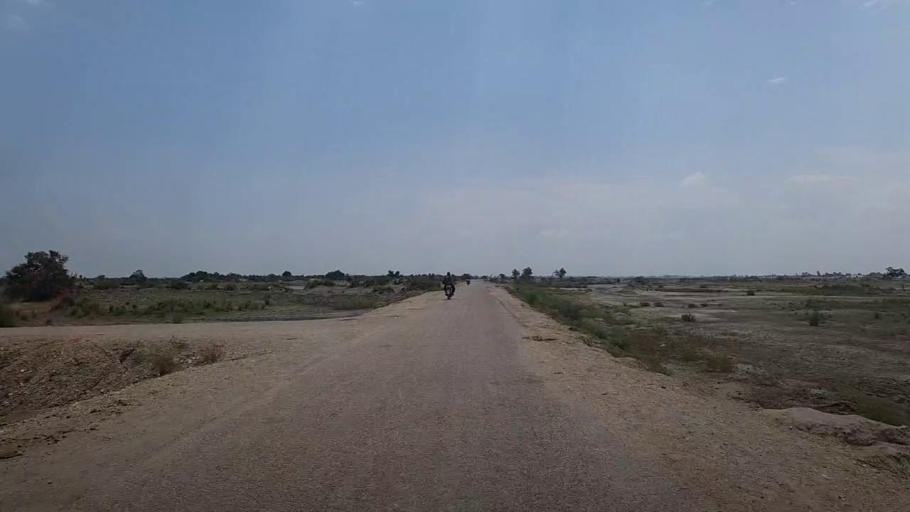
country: PK
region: Sindh
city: Kandhkot
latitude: 28.2909
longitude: 69.1440
